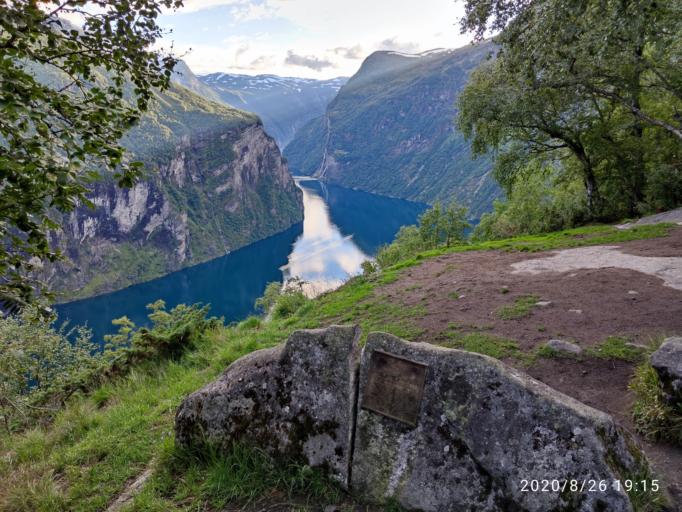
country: NO
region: More og Romsdal
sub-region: Norddal
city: Valldal
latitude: 62.1266
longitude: 7.1659
